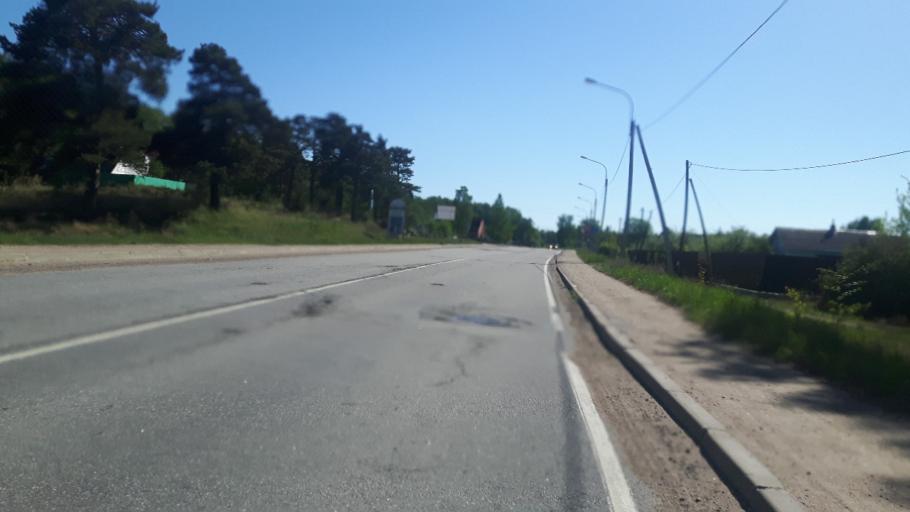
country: RU
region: Leningrad
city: Sosnovyy Bor
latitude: 60.2185
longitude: 29.0101
